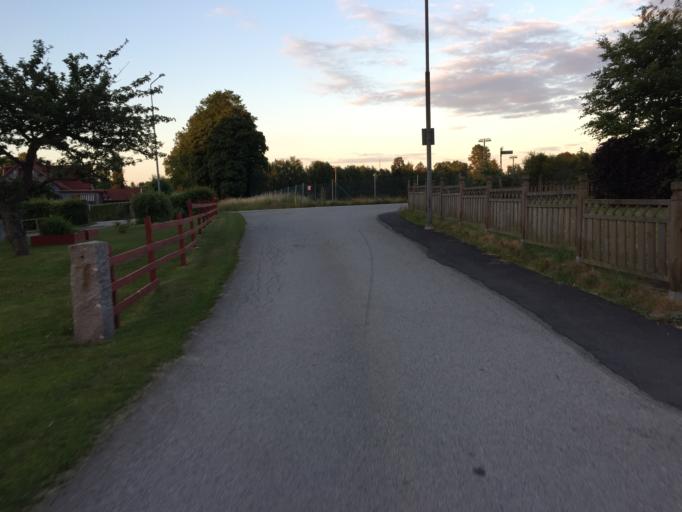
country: SE
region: Skane
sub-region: Hassleholms Kommun
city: Sosdala
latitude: 56.0448
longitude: 13.6829
